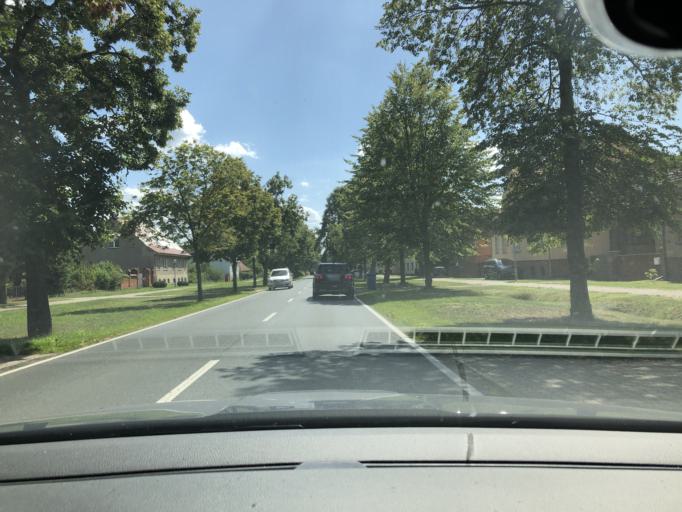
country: DE
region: Brandenburg
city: Ruthnick
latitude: 52.9002
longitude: 12.9719
